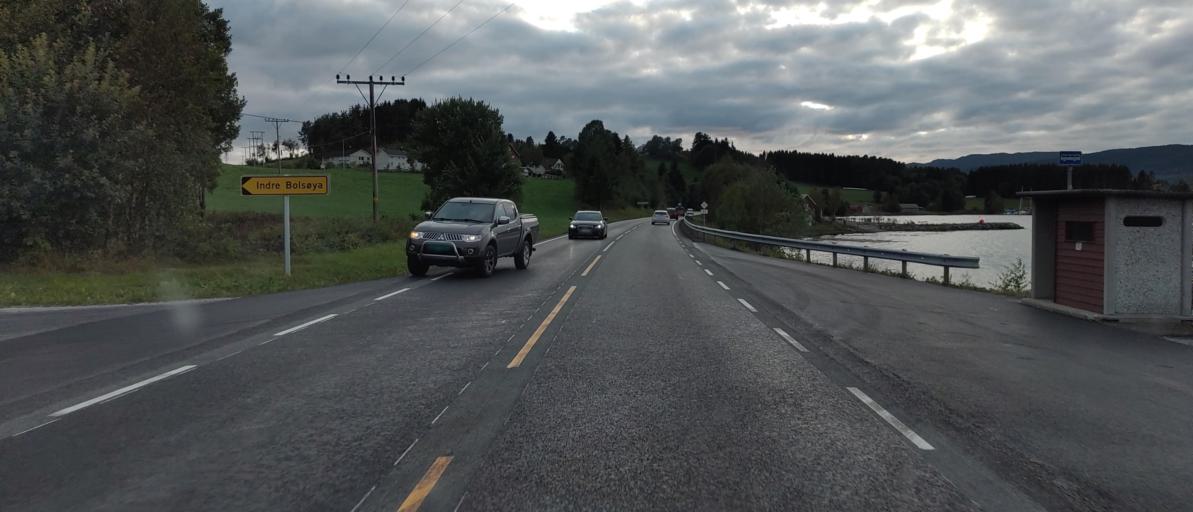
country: NO
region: More og Romsdal
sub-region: Molde
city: Hjelset
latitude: 62.7317
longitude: 7.3398
